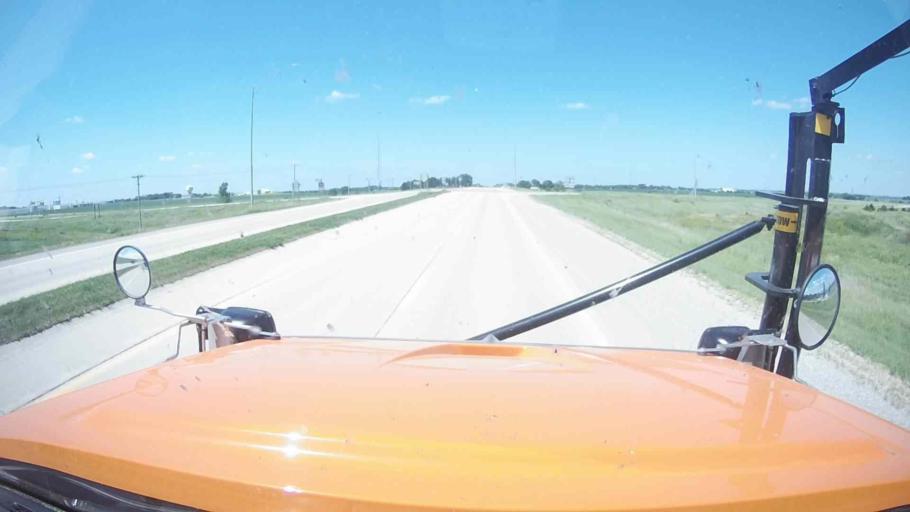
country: US
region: Iowa
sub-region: Cerro Gordo County
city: Mason City
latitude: 43.1019
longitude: -93.2013
